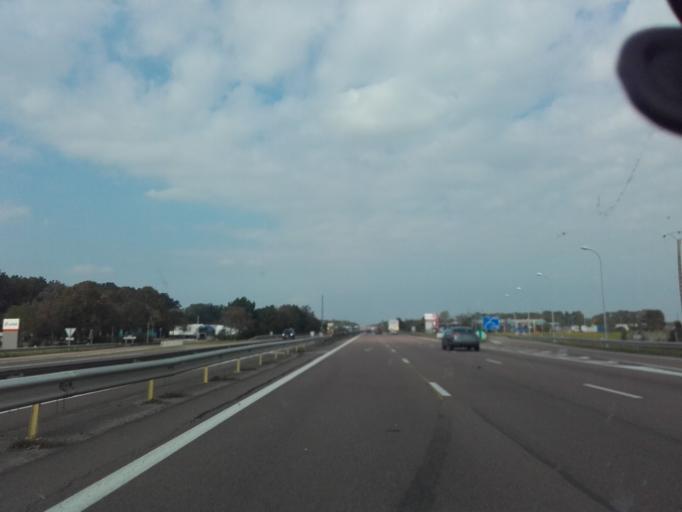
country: FR
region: Bourgogne
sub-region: Departement de Saone-et-Loire
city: Varennes-le-Grand
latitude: 46.6884
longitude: 4.8445
